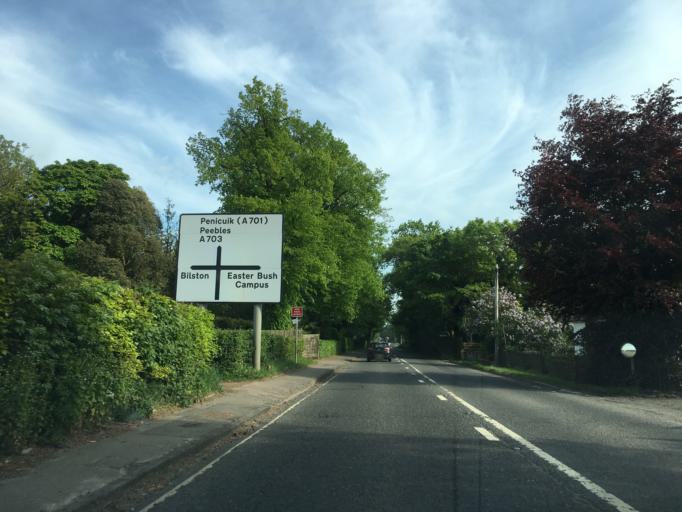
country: GB
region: Scotland
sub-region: Midlothian
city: Loanhead
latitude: 55.8716
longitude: -3.1924
